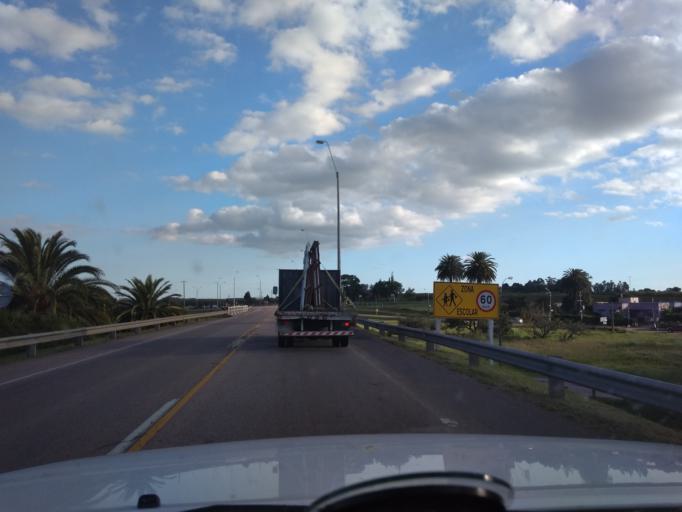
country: UY
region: Canelones
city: Canelones
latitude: -34.5428
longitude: -56.2743
